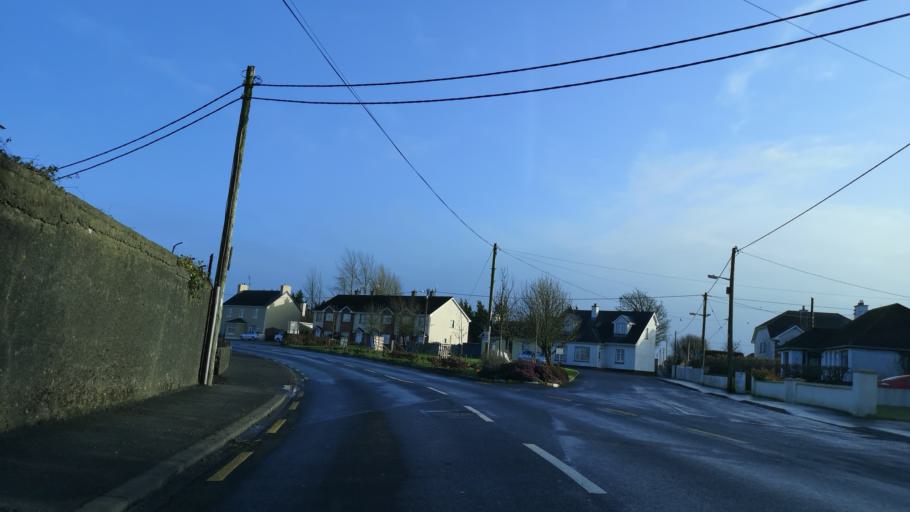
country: IE
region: Connaught
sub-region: County Galway
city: Tuam
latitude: 53.5066
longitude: -8.8377
